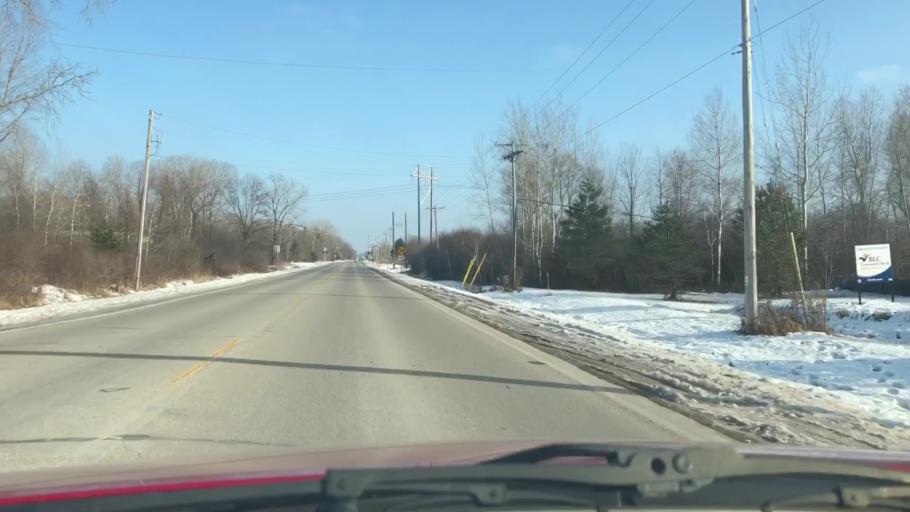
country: US
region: Wisconsin
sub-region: Outagamie County
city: Appleton
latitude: 44.3169
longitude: -88.4387
